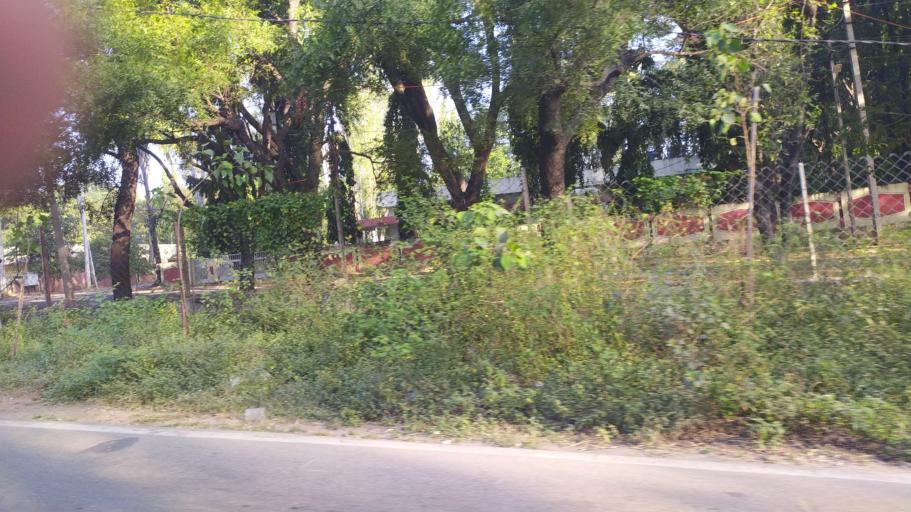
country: IN
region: Telangana
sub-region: Hyderabad
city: Hyderabad
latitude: 17.3294
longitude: 78.4146
